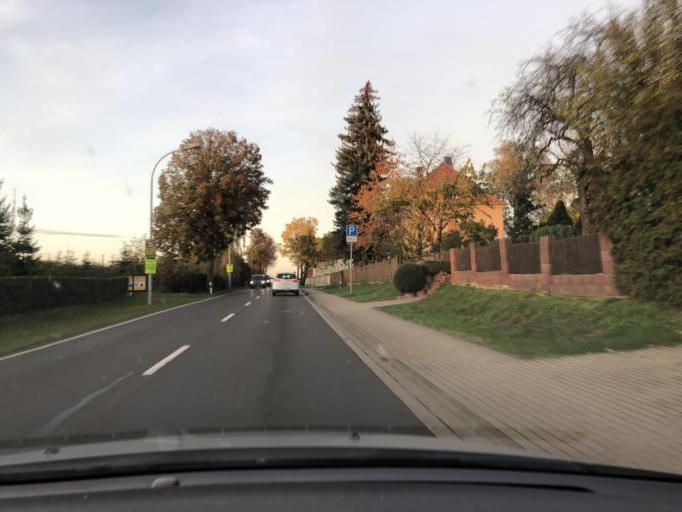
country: DE
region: Saxony
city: Groitzsch
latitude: 51.1734
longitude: 12.2900
